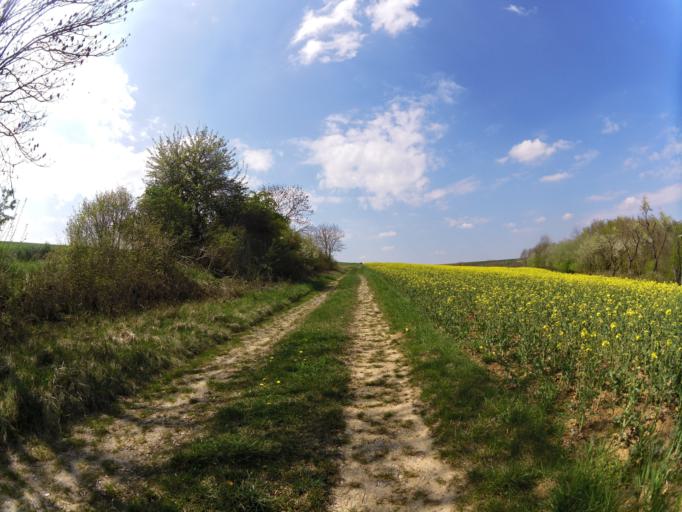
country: DE
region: Bavaria
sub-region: Regierungsbezirk Unterfranken
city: Sommerhausen
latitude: 49.6850
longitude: 10.0162
